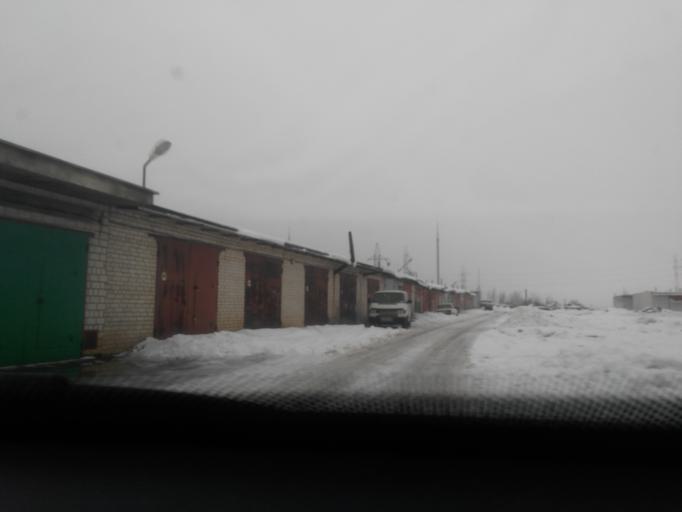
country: BY
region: Mogilev
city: Babruysk
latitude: 53.1933
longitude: 29.2174
